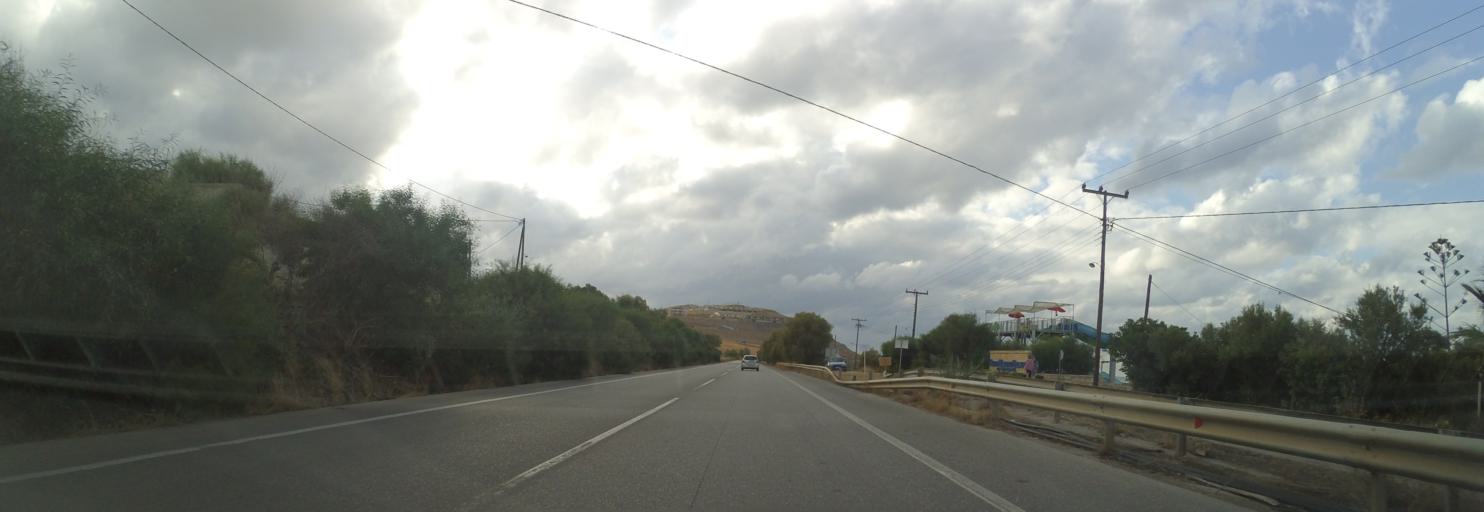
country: GR
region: Crete
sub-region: Nomos Rethymnis
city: Panormos
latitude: 35.4160
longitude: 24.6855
